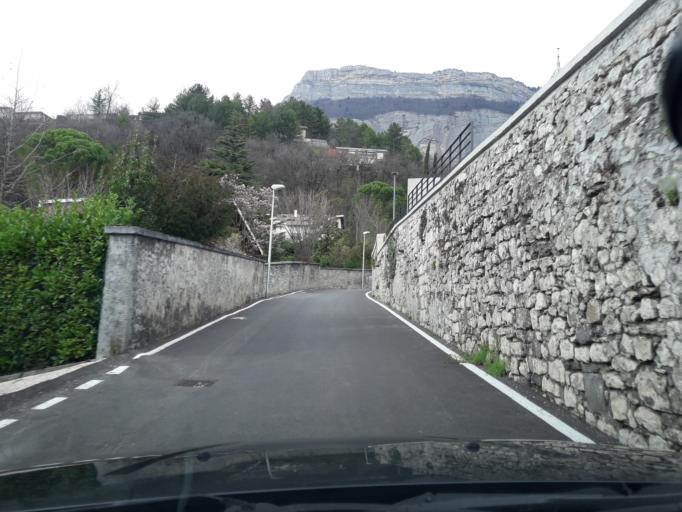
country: FR
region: Rhone-Alpes
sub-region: Departement de l'Isere
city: Corenc
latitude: 45.2185
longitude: 5.7741
